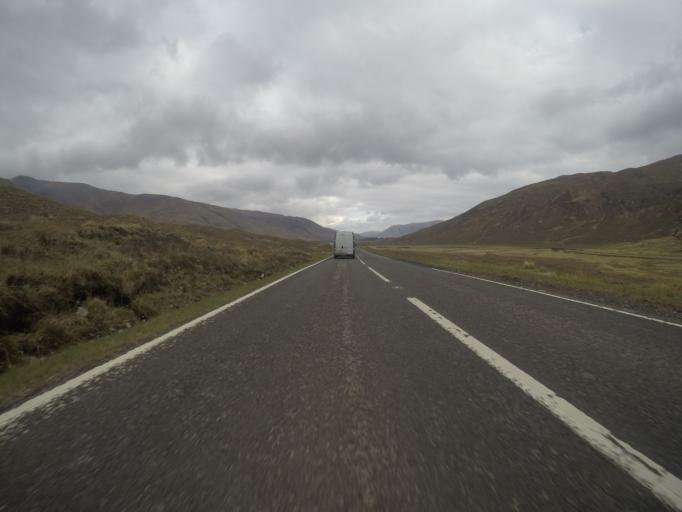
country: GB
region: Scotland
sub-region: Highland
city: Fort William
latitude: 57.1536
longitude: -5.1943
